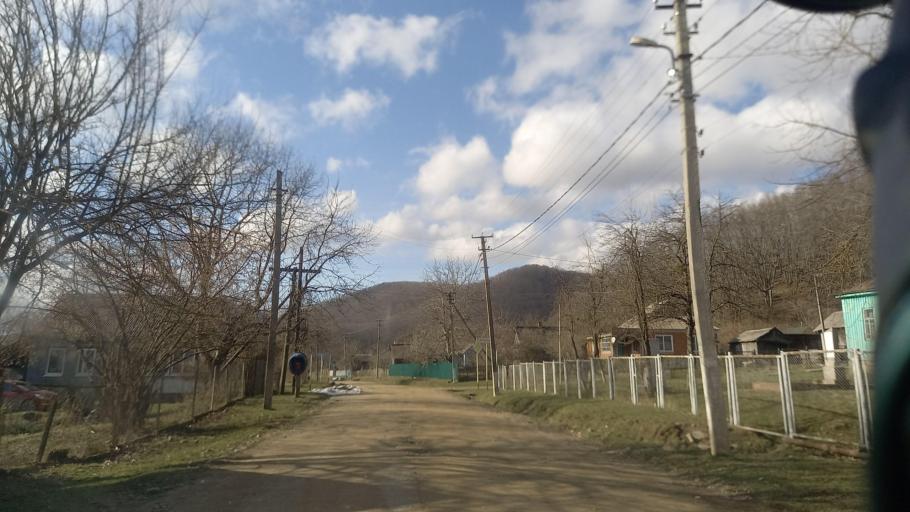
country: RU
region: Krasnodarskiy
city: Smolenskaya
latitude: 44.6039
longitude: 38.8567
